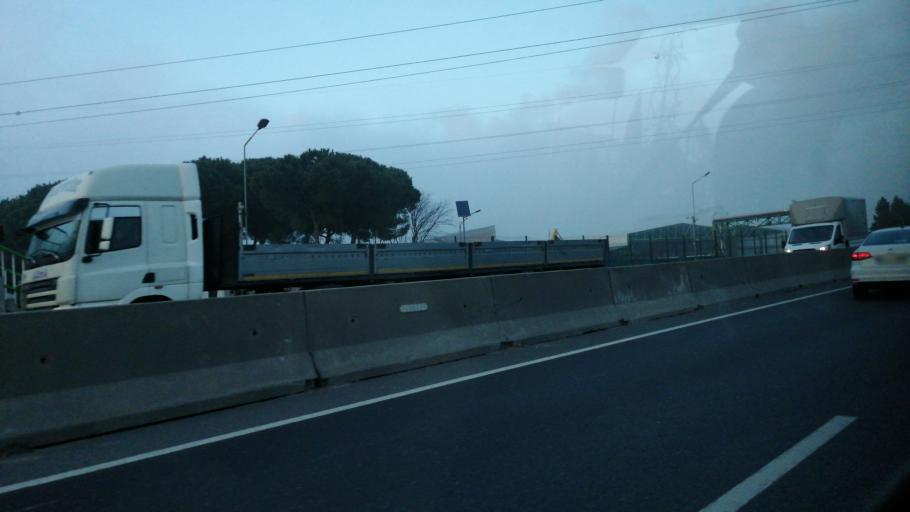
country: TR
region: Yalova
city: Taskopru
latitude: 40.6837
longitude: 29.4052
